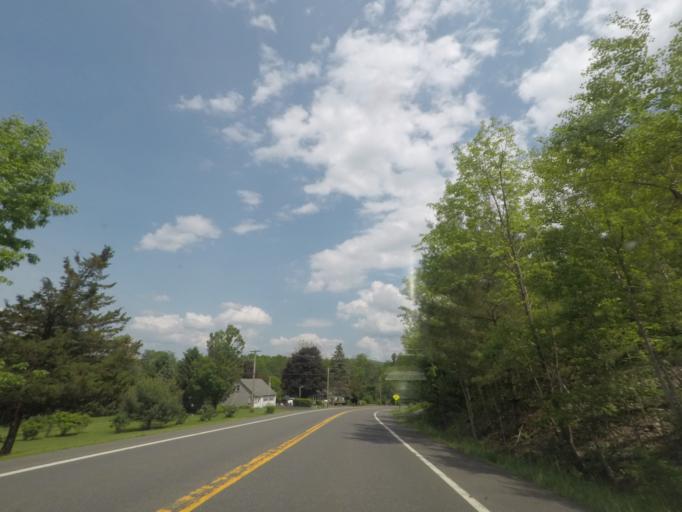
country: US
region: New York
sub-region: Dutchess County
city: Pine Plains
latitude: 42.1100
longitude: -73.6975
